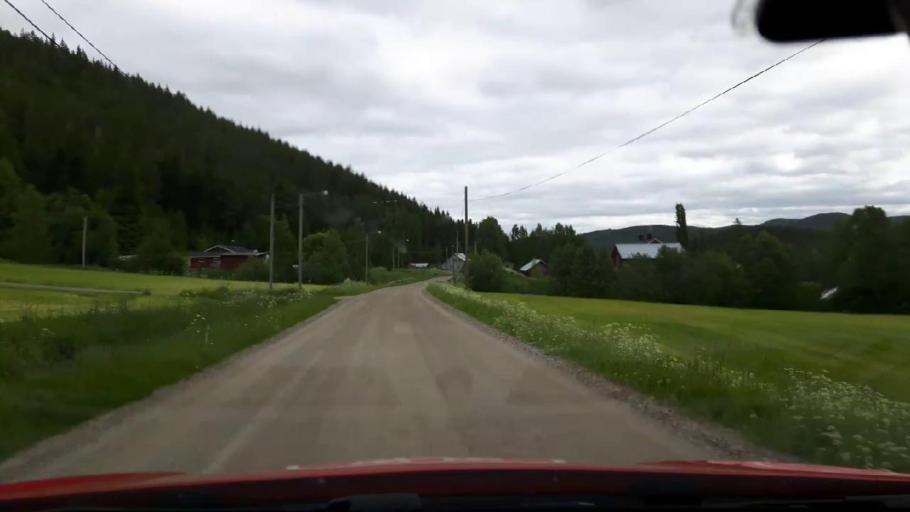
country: SE
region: Jaemtland
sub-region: Ragunda Kommun
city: Hammarstrand
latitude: 63.1728
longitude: 16.2030
